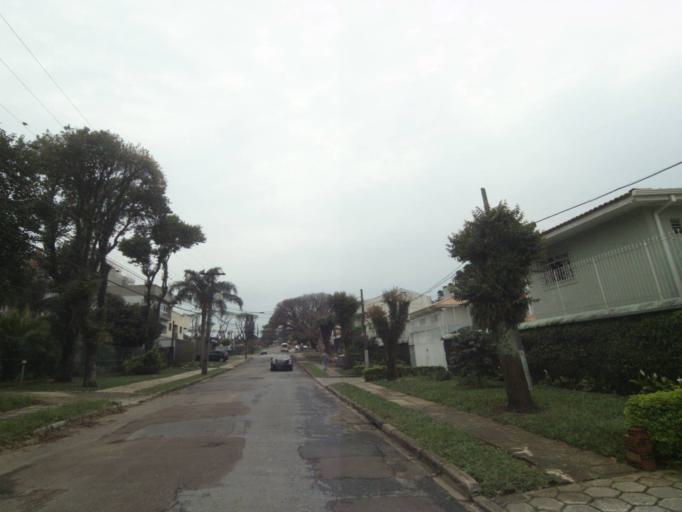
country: BR
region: Parana
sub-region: Curitiba
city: Curitiba
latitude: -25.4788
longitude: -49.3015
